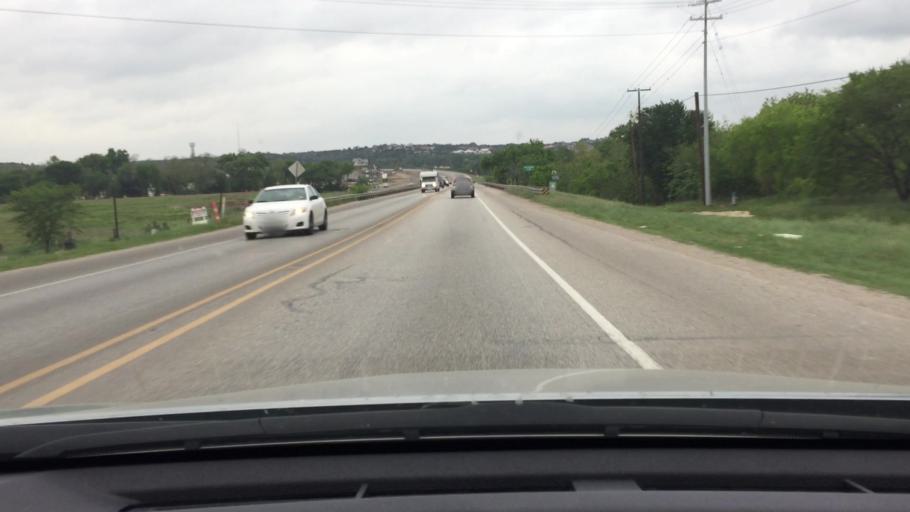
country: US
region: Texas
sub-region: Comal County
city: New Braunfels
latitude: 29.6865
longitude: -98.1549
